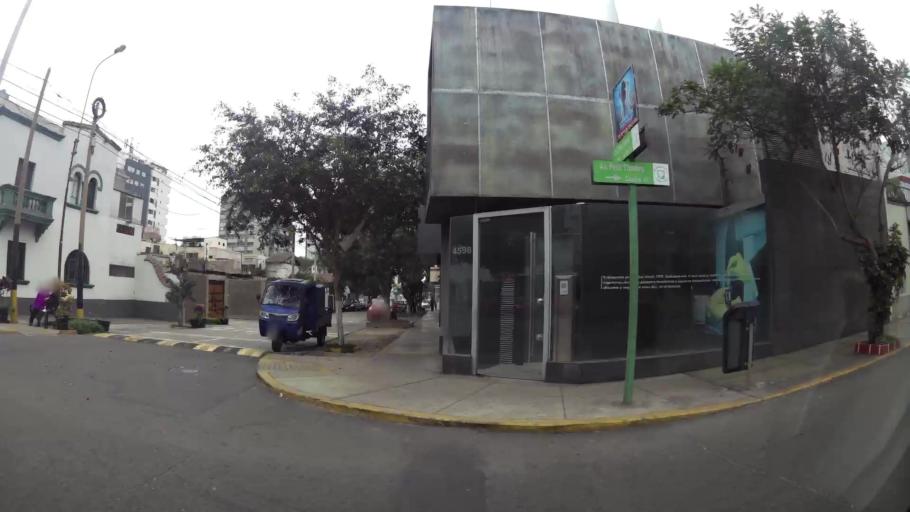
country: PE
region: Lima
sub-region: Lima
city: San Isidro
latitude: -12.1085
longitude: -77.0296
